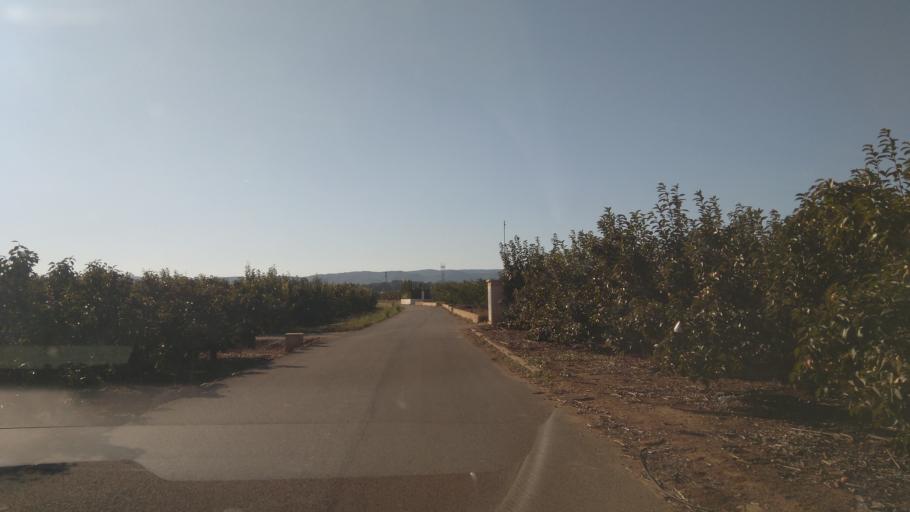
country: ES
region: Valencia
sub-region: Provincia de Valencia
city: Masalaves
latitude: 39.1769
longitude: -0.5418
